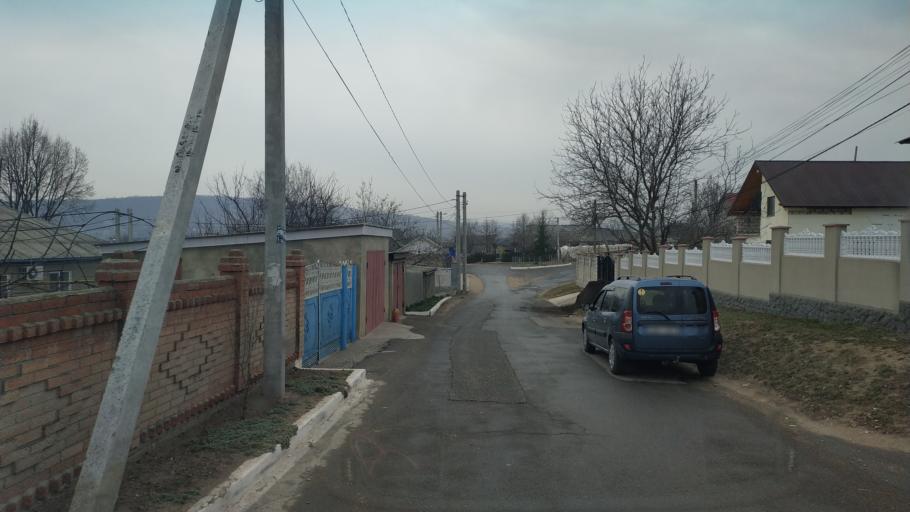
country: MD
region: Chisinau
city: Singera
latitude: 46.9176
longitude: 28.9592
